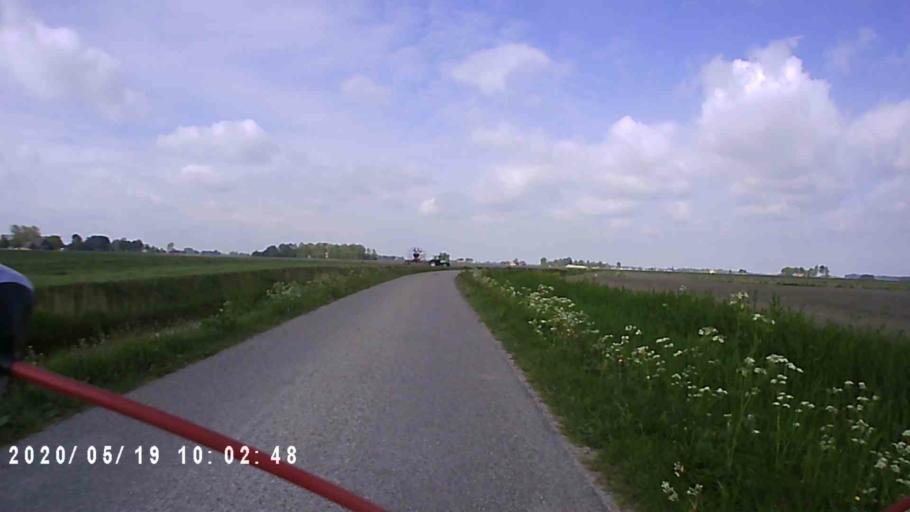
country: NL
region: Groningen
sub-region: Gemeente Zuidhorn
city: Grijpskerk
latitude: 53.3032
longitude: 6.2339
